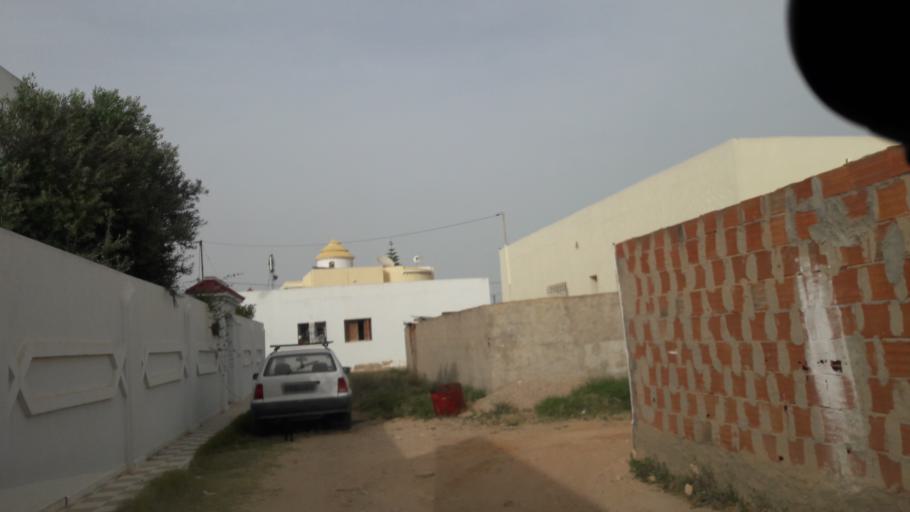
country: TN
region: Safaqis
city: Al Qarmadah
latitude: 34.7803
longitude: 10.7707
